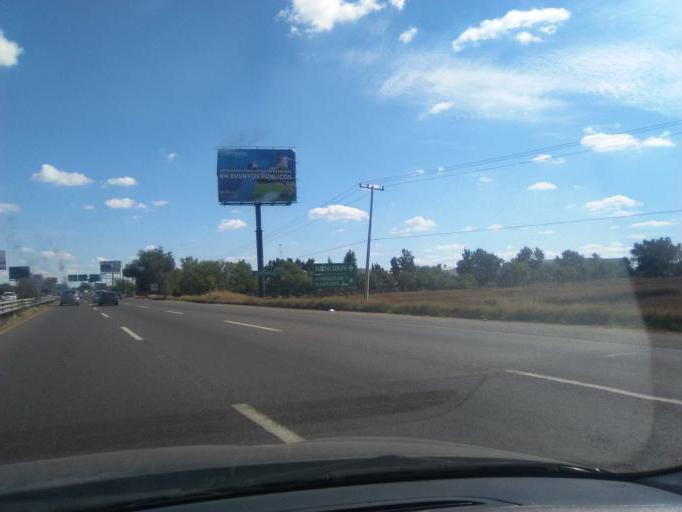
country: MX
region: Guanajuato
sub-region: Leon
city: Ladrilleras del Refugio
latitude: 21.0531
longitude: -101.5746
